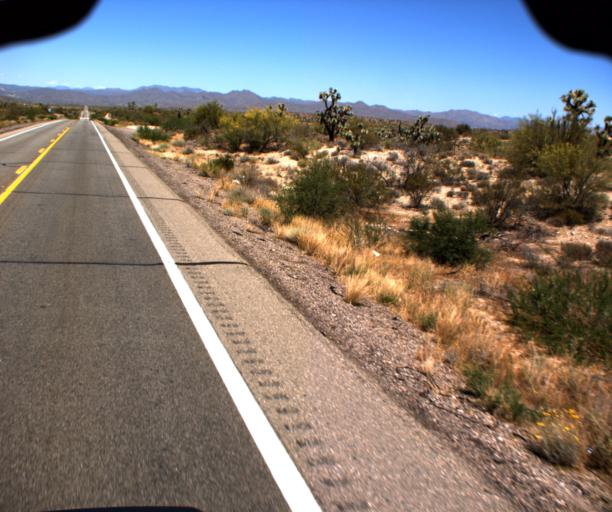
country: US
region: Arizona
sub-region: Yavapai County
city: Bagdad
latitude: 34.3116
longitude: -113.1275
